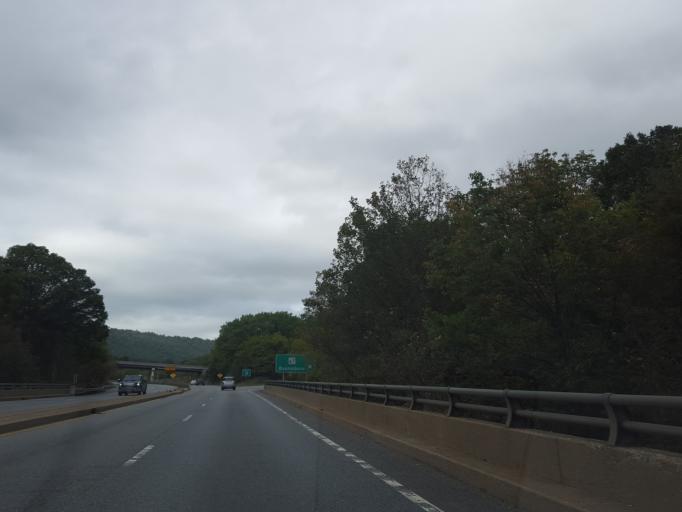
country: US
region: Maryland
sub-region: Frederick County
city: Brunswick
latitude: 39.3315
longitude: -77.6855
